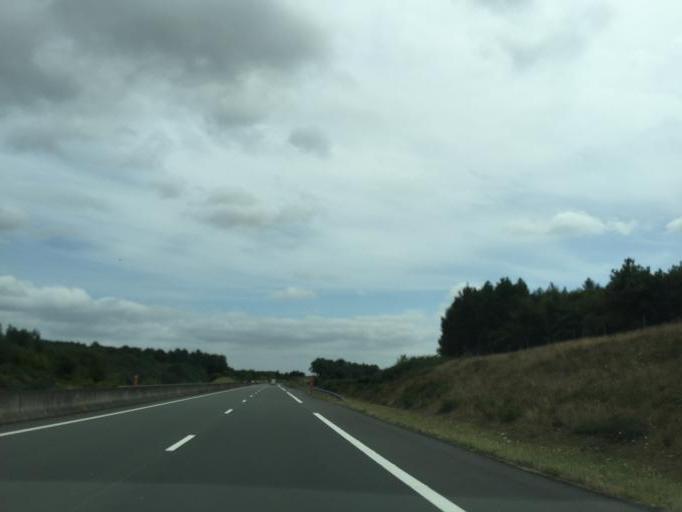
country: FR
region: Pays de la Loire
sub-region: Departement de la Sarthe
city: Vaas
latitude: 47.7273
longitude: 0.3358
